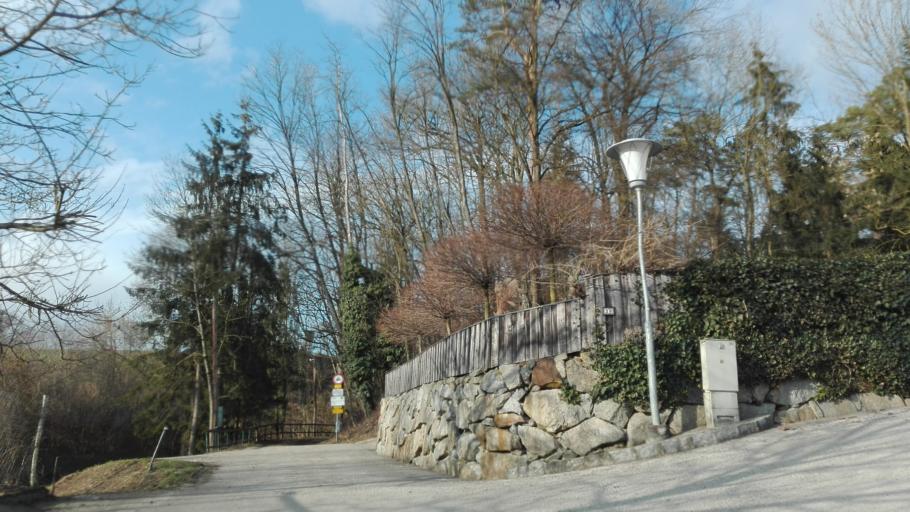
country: AT
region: Upper Austria
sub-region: Politischer Bezirk Perg
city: Perg
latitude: 48.2552
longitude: 14.6169
